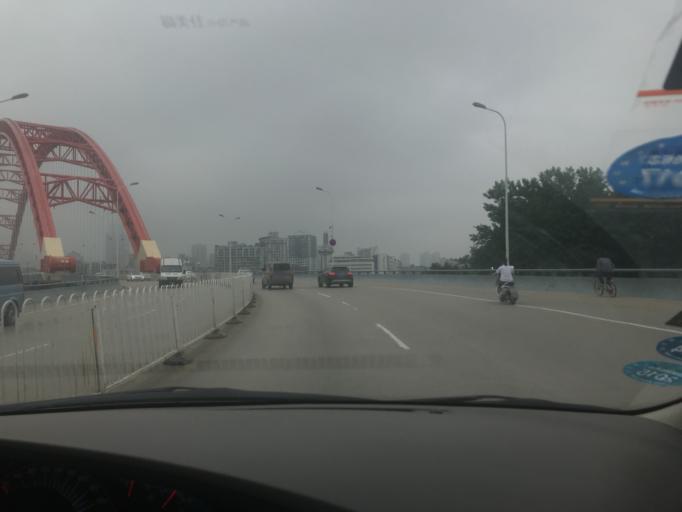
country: CN
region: Hubei
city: Wuhan
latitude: 30.5640
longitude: 114.2806
